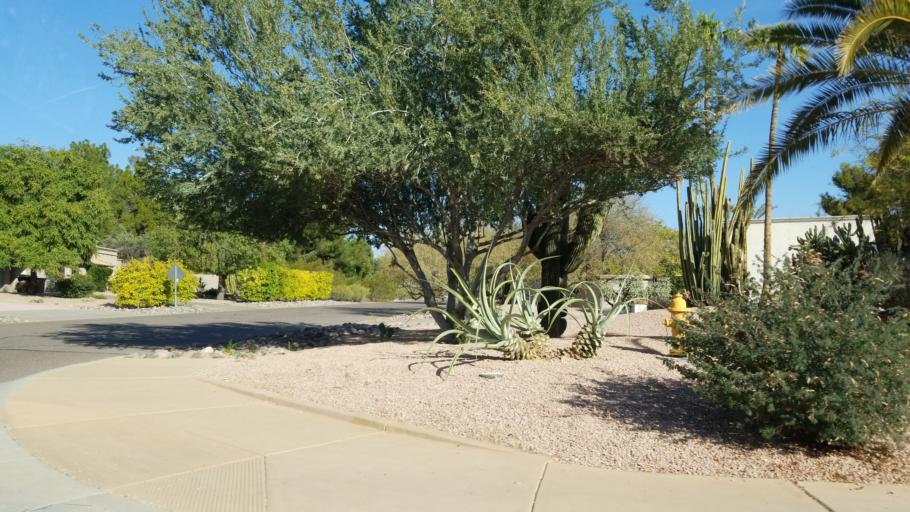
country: US
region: Arizona
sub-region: Maricopa County
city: Paradise Valley
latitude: 33.5677
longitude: -111.9461
